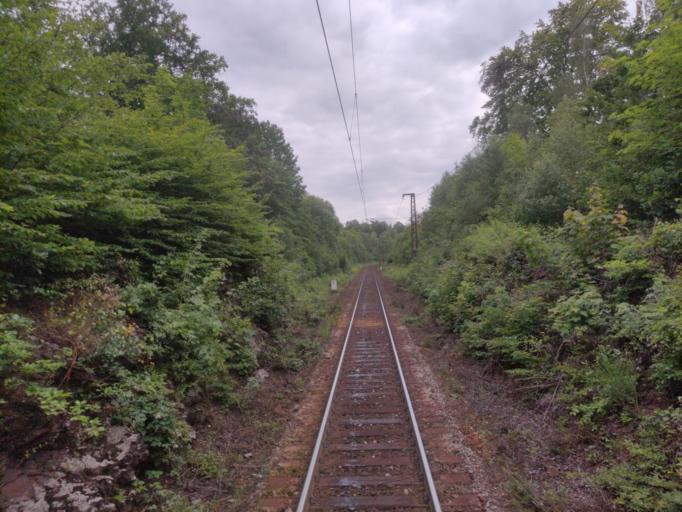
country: DE
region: Saxony-Anhalt
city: Huttenrode
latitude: 51.7876
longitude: 10.9239
